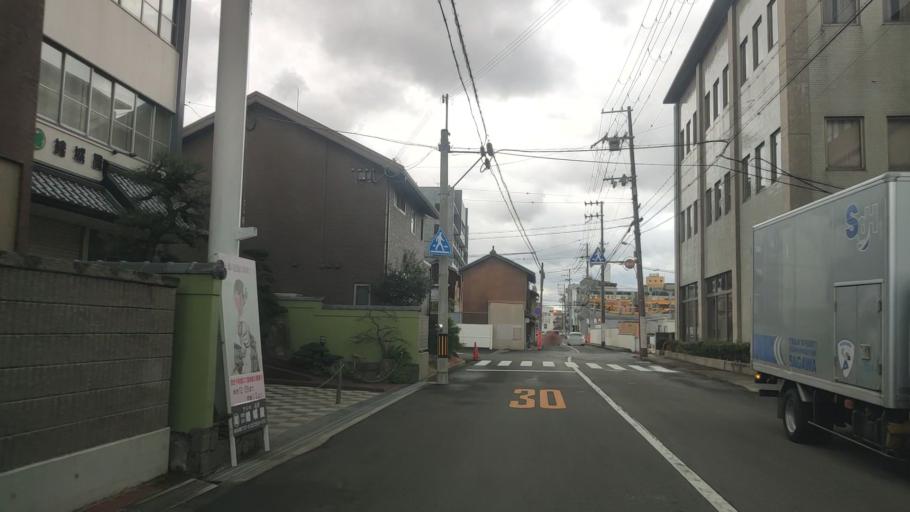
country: JP
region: Hyogo
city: Sumoto
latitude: 34.3440
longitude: 134.8965
